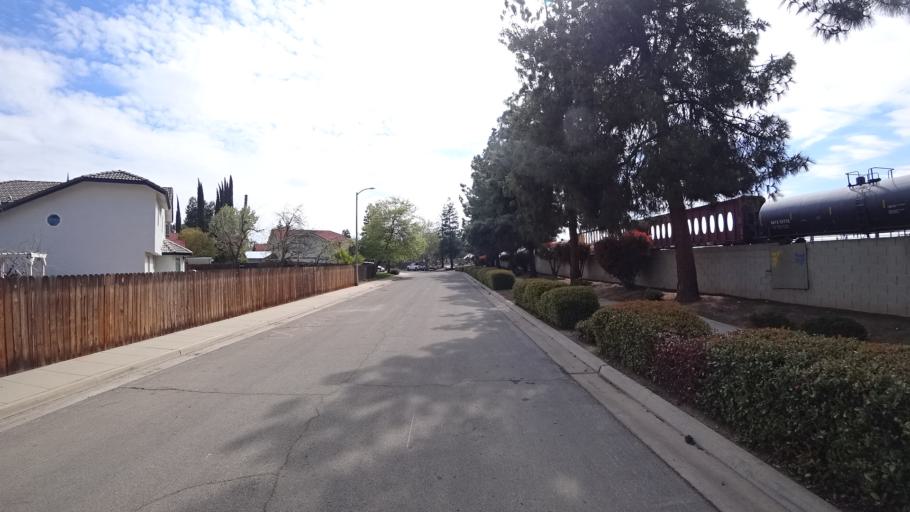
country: US
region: California
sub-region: Fresno County
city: West Park
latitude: 36.8182
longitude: -119.8562
